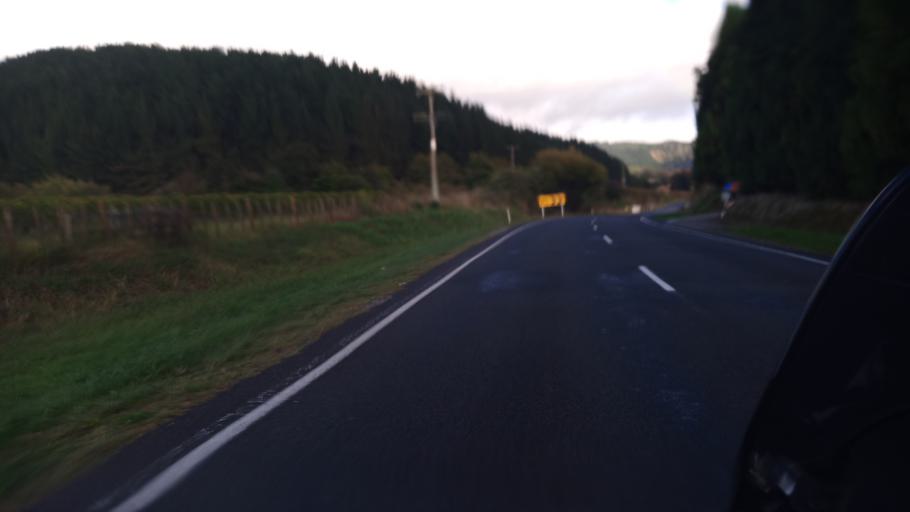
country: NZ
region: Gisborne
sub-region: Gisborne District
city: Gisborne
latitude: -38.6349
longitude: 177.8540
